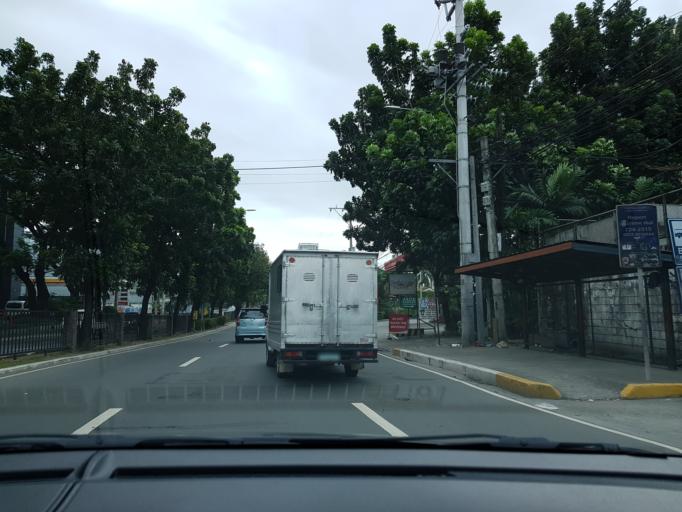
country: PH
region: Metro Manila
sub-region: San Juan
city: San Juan
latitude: 14.6072
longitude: 121.0396
